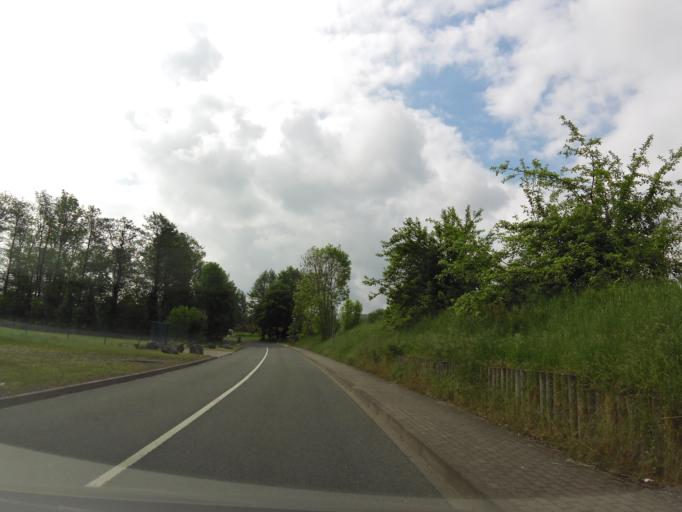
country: DE
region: Thuringia
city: Horselgau
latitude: 50.9295
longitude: 10.5739
